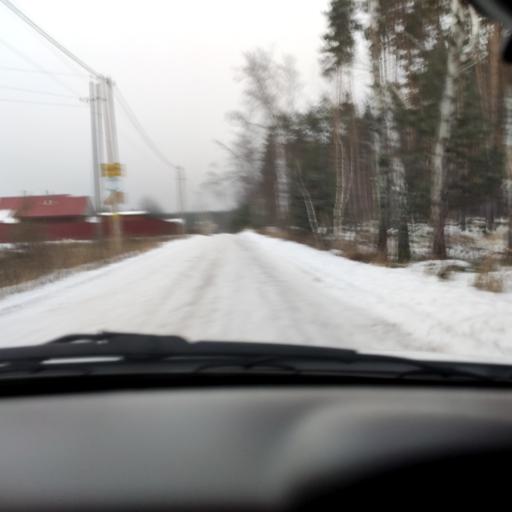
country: RU
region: Voronezj
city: Ramon'
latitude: 51.8832
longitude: 39.2622
